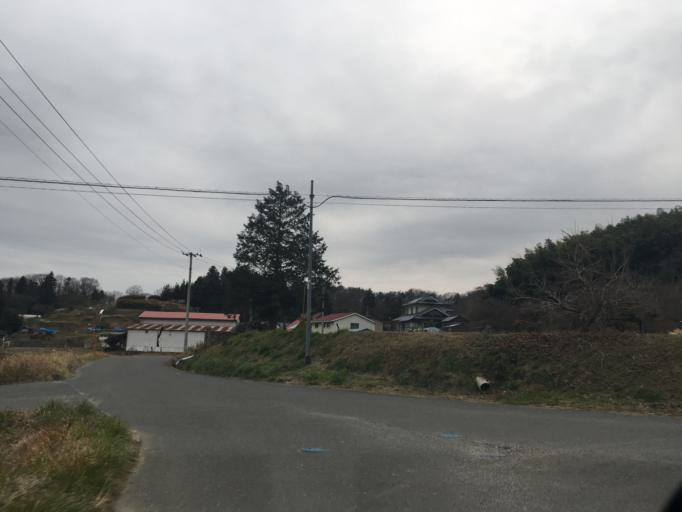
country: JP
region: Fukushima
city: Sukagawa
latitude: 37.3411
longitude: 140.4377
